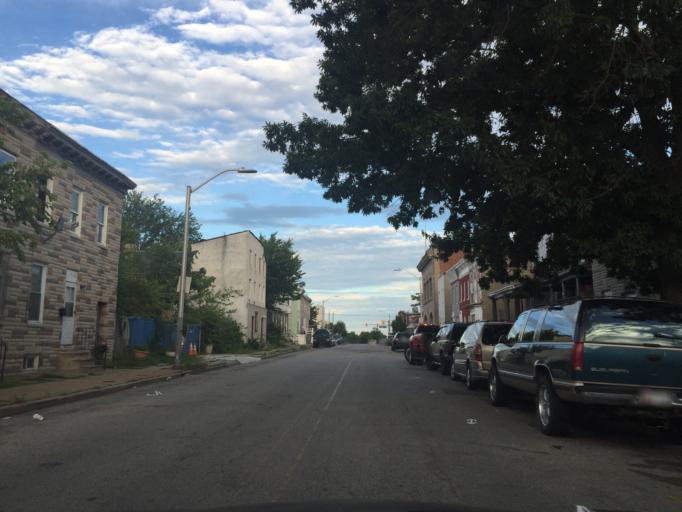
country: US
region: Maryland
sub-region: City of Baltimore
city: Baltimore
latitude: 39.3206
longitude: -76.5937
